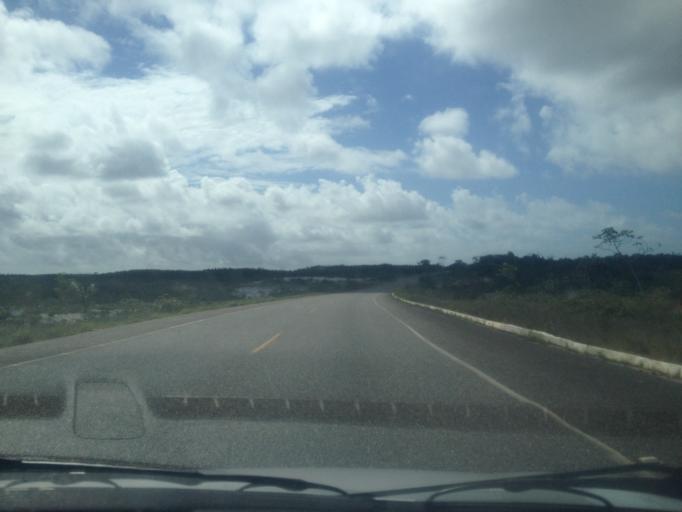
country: BR
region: Bahia
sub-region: Entre Rios
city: Entre Rios
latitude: -12.2461
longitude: -37.8582
